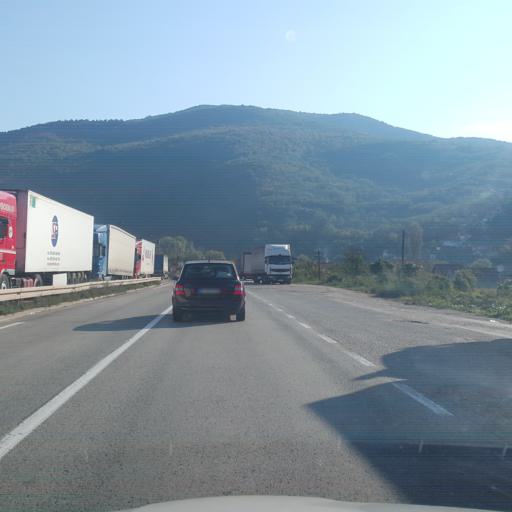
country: RS
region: Central Serbia
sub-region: Nisavski Okrug
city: Niska Banja
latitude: 43.3115
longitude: 22.0463
